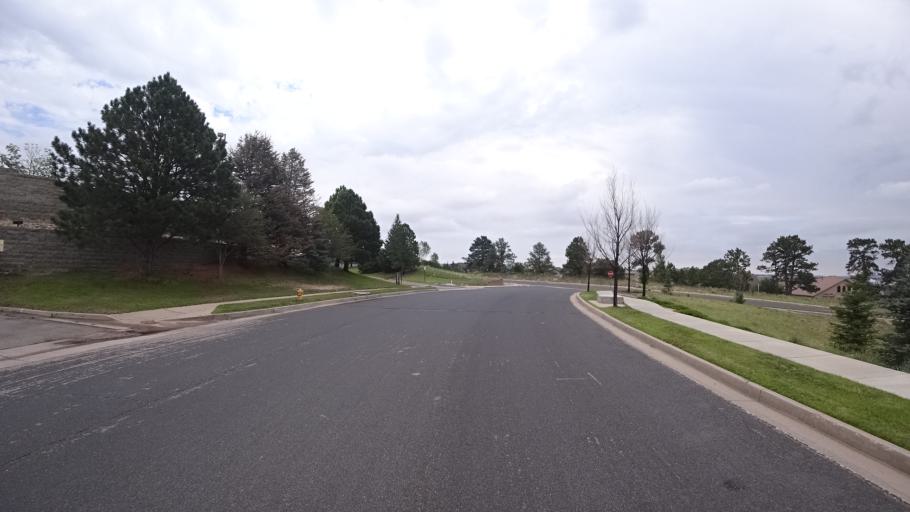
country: US
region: Colorado
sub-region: El Paso County
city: Gleneagle
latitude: 39.0043
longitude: -104.7939
